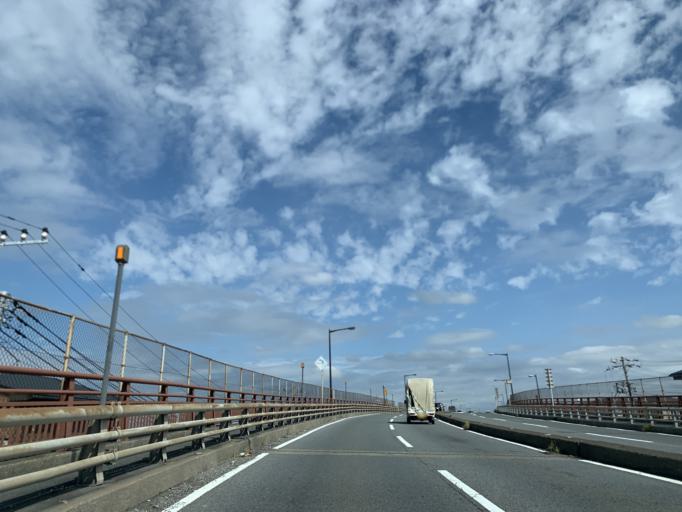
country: JP
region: Tokyo
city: Urayasu
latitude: 35.6994
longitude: 139.9240
